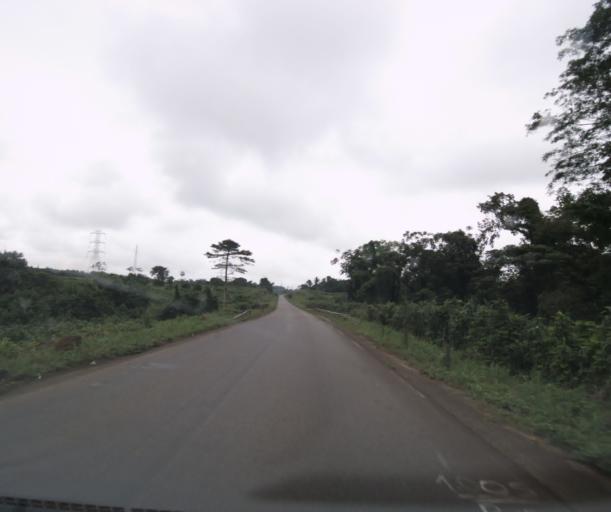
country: CM
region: Littoral
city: Edea
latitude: 3.6926
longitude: 10.1045
